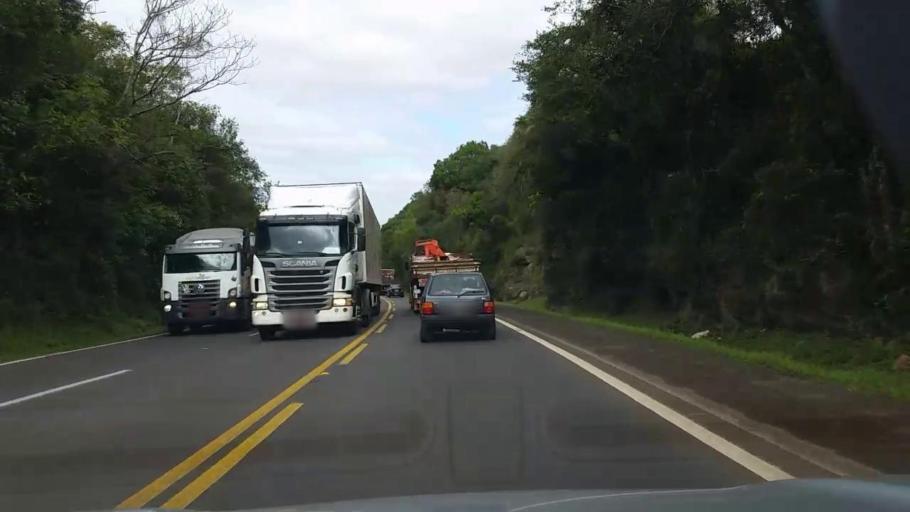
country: BR
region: Rio Grande do Sul
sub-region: Arroio Do Meio
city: Arroio do Meio
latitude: -29.3951
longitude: -52.0426
